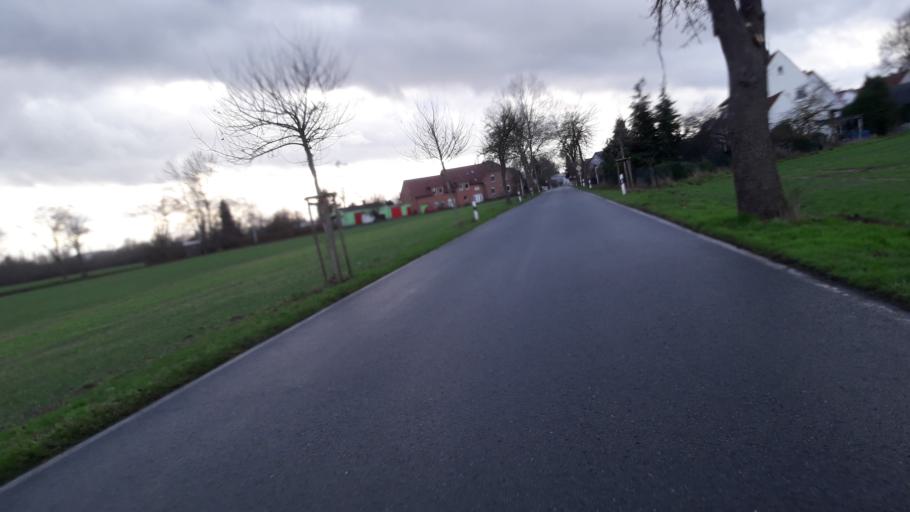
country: DE
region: North Rhine-Westphalia
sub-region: Regierungsbezirk Detmold
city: Petershagen
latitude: 52.3168
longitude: 8.9714
